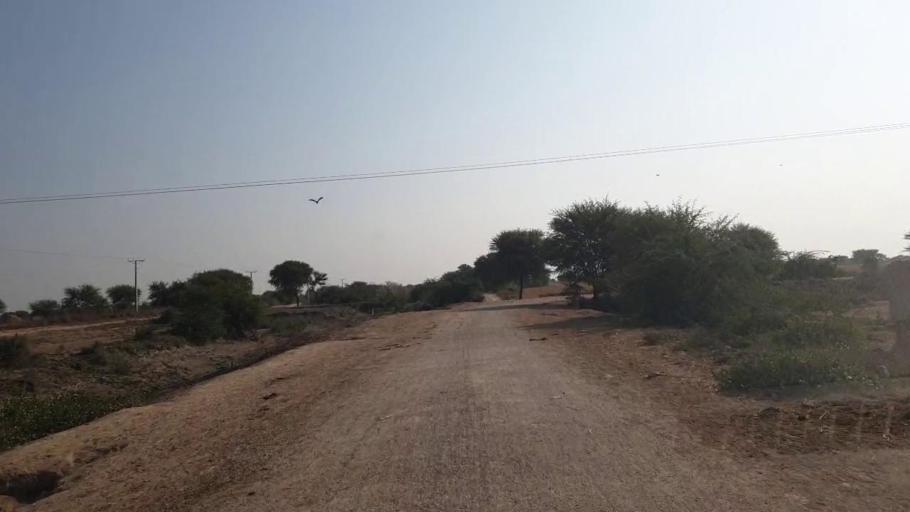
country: PK
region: Sindh
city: Kario
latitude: 24.8925
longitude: 68.6476
